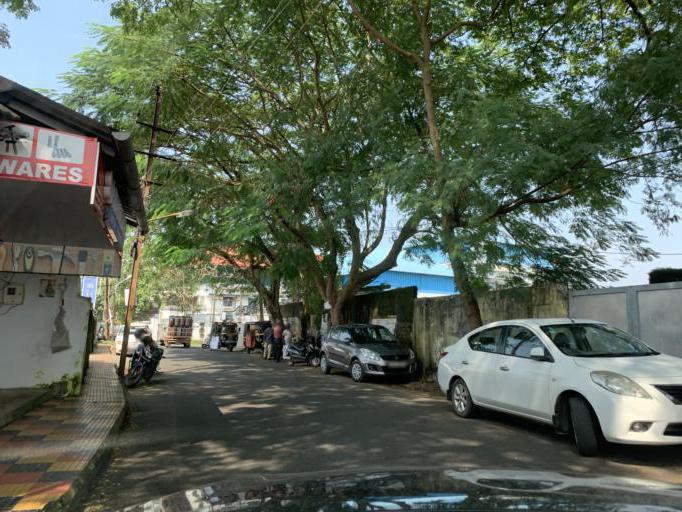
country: IN
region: Kerala
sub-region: Ernakulam
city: Cochin
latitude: 9.9451
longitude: 76.2610
